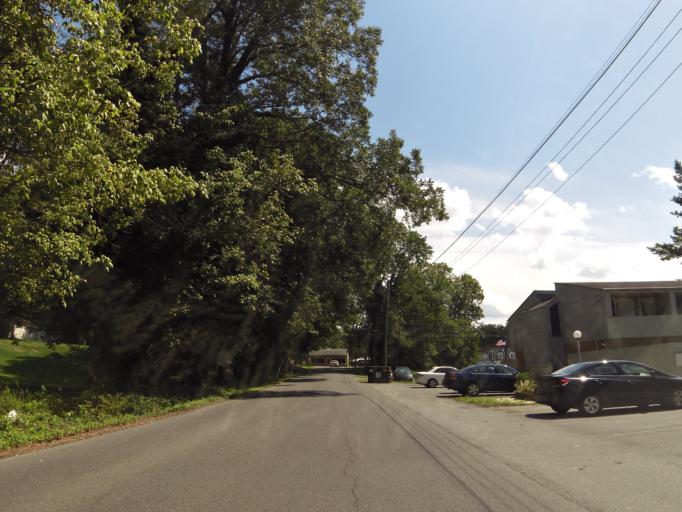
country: US
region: Virginia
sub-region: Washington County
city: Abingdon
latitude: 36.7158
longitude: -81.9635
